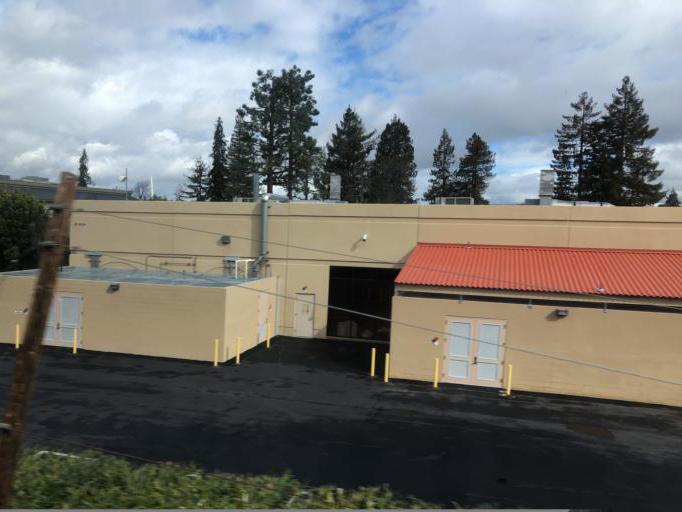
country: US
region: California
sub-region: Santa Clara County
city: Santa Clara
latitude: 37.3681
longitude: -121.9700
